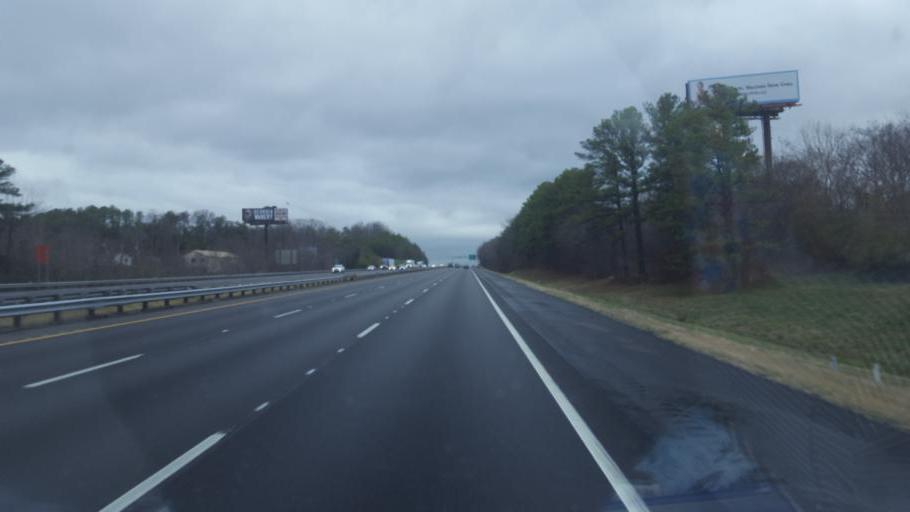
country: US
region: Georgia
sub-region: Catoosa County
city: Ringgold
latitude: 34.9191
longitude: -85.1472
